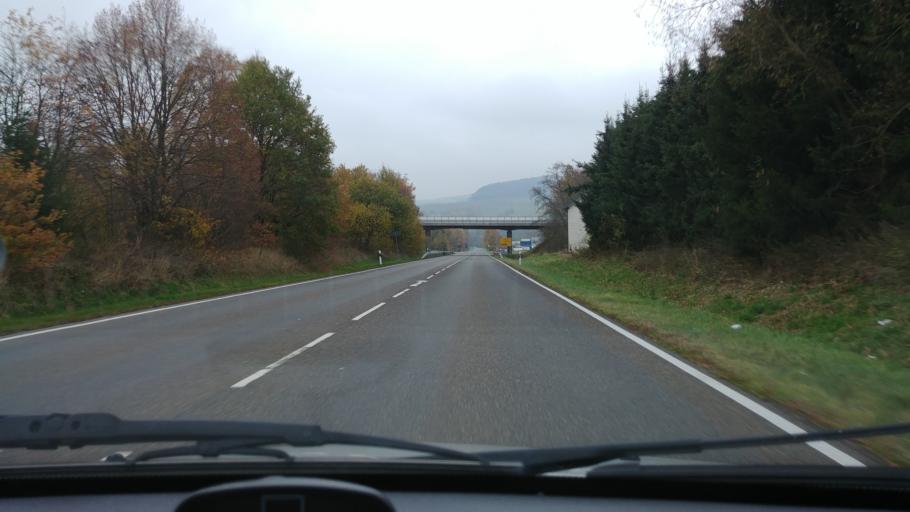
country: DE
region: Rheinland-Pfalz
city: Enspel
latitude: 50.6261
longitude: 7.8859
